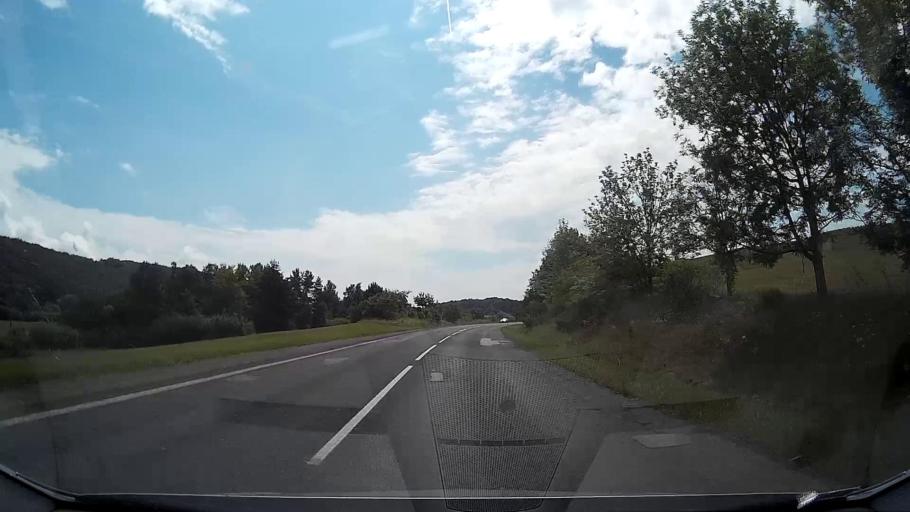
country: SK
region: Banskobystricky
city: Rimavska Sobota
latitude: 48.4849
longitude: 19.9445
